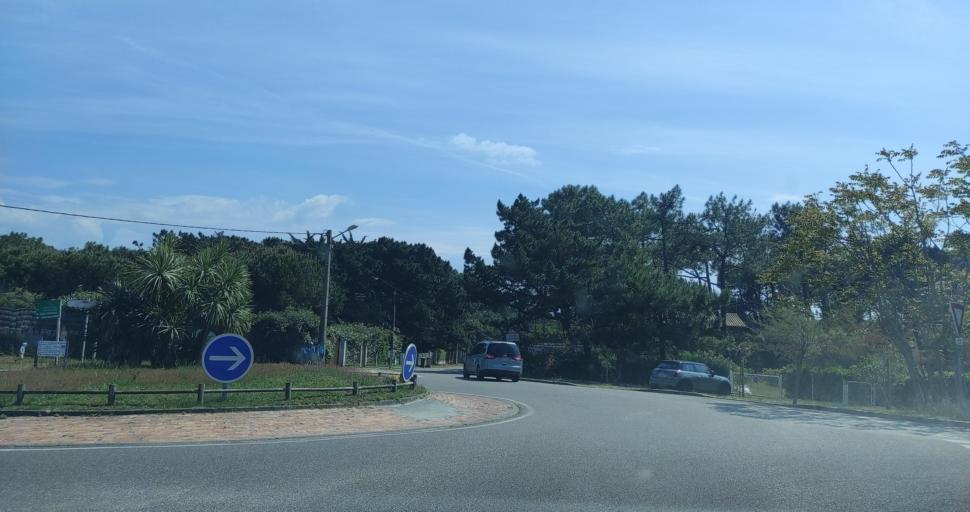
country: FR
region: Aquitaine
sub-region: Departement de la Gironde
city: Arcachon
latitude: 44.6456
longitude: -1.2541
